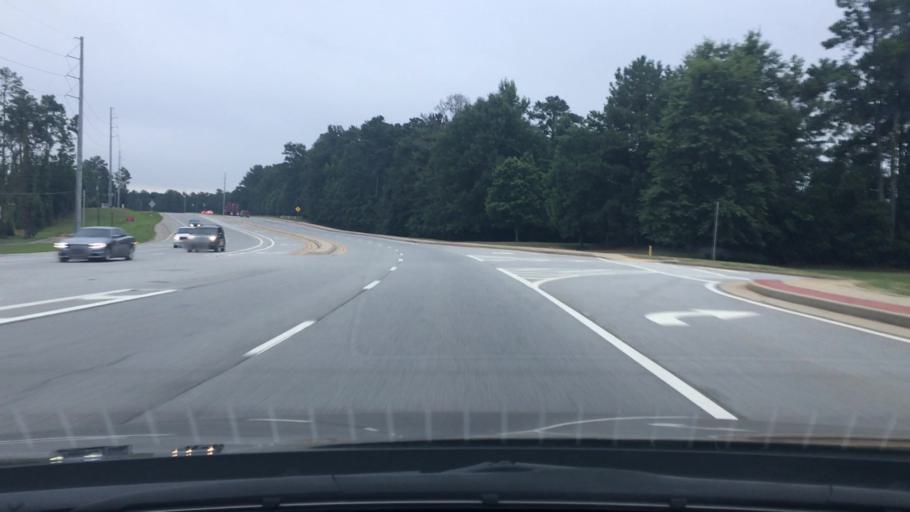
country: US
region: Georgia
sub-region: Coweta County
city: Senoia
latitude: 33.3454
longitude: -84.5469
